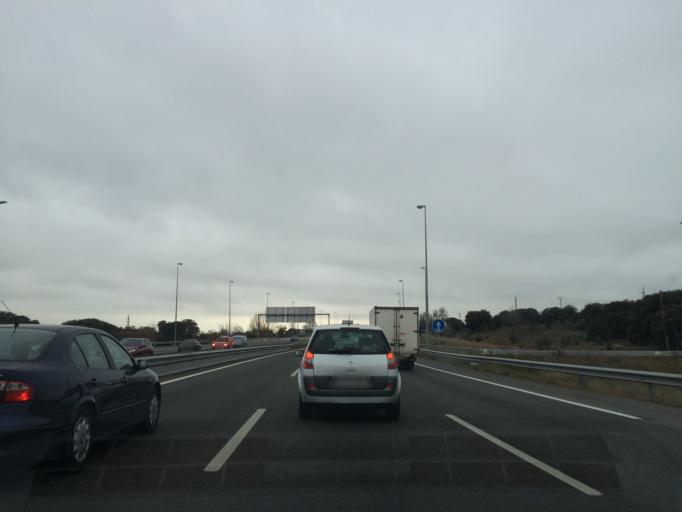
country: ES
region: Madrid
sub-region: Provincia de Madrid
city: Tres Cantos
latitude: 40.5828
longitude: -3.7060
